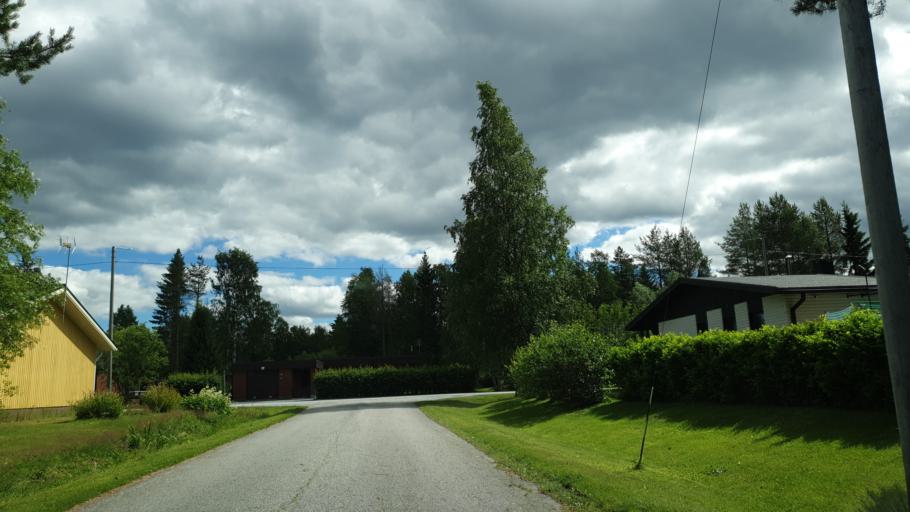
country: FI
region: Kainuu
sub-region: Kehys-Kainuu
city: Kuhmo
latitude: 64.1147
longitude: 29.4793
